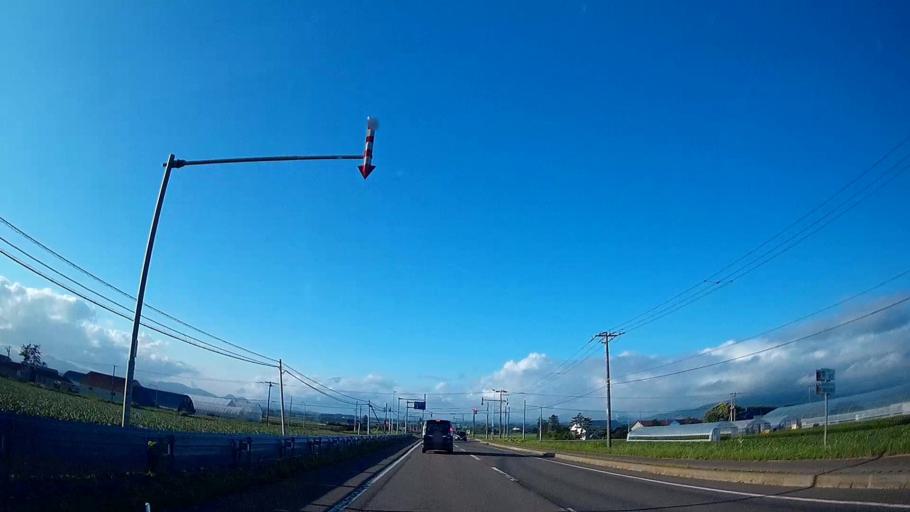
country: JP
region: Hokkaido
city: Date
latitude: 42.6328
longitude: 140.8008
